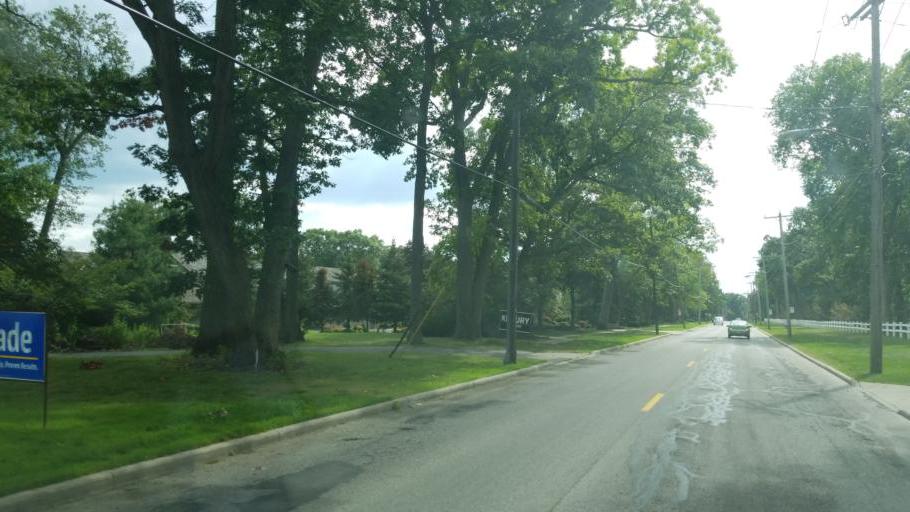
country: US
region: Ohio
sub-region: Wood County
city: Rossford
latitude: 41.5975
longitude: -83.5962
